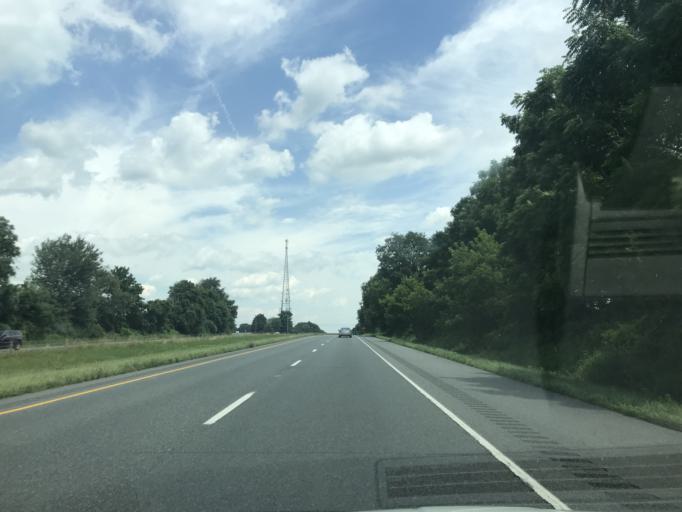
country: US
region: Pennsylvania
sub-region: Chester County
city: Oxford
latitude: 39.8194
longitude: -75.9195
